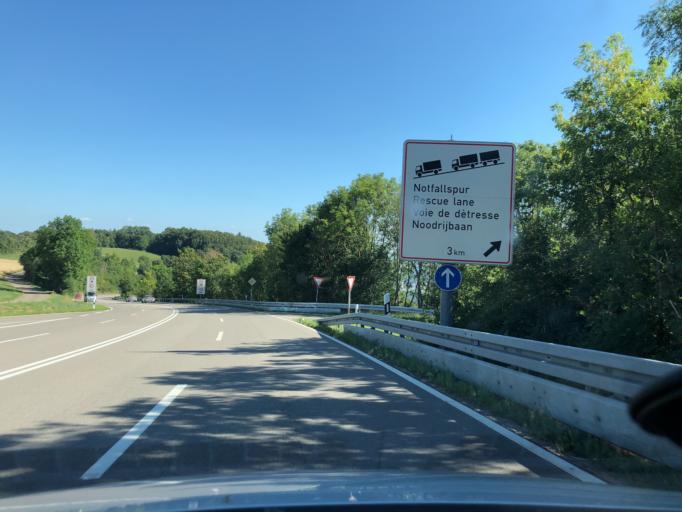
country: DE
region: Baden-Wuerttemberg
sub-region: Freiburg Region
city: Dogern
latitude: 47.6507
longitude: 8.1754
